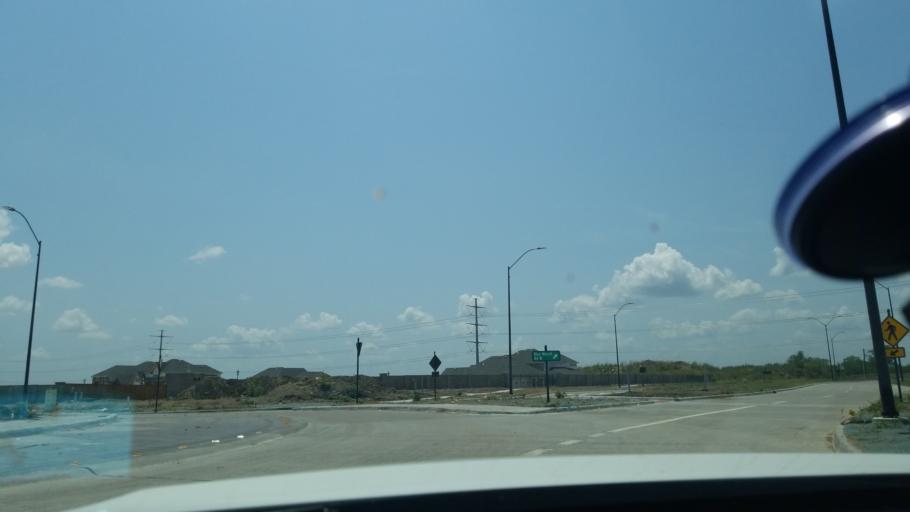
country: US
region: Texas
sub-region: Tarrant County
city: Haslet
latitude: 32.9446
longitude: -97.3982
